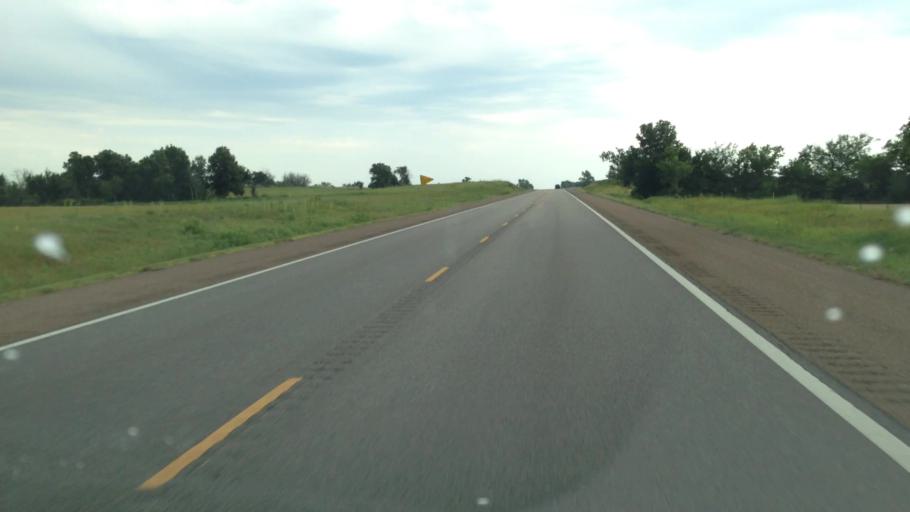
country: US
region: Kansas
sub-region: Woodson County
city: Yates Center
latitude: 38.0201
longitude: -95.7392
